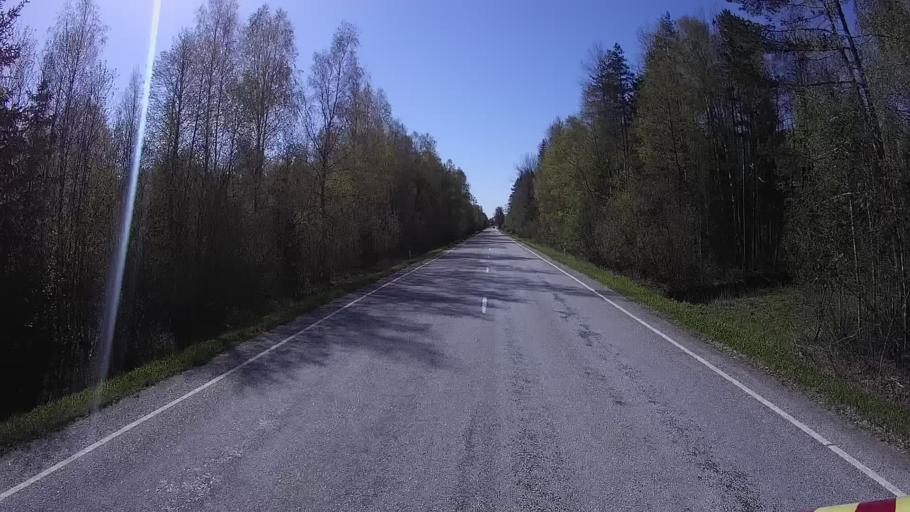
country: EE
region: Raplamaa
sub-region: Jaervakandi vald
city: Jarvakandi
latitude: 58.8000
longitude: 24.8142
